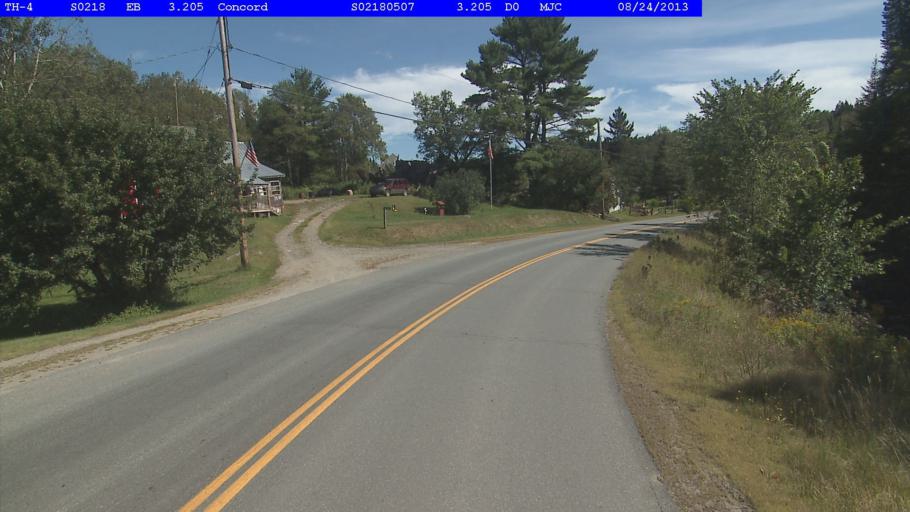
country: US
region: New Hampshire
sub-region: Grafton County
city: Littleton
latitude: 44.4239
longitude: -71.7522
